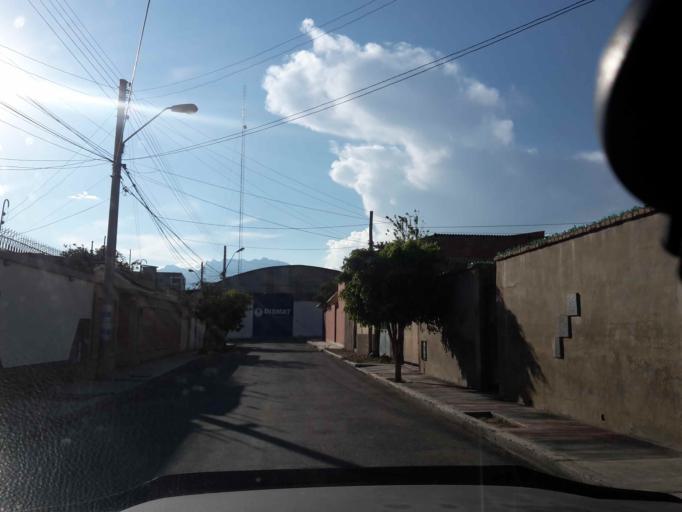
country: BO
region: Cochabamba
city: Cochabamba
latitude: -17.3478
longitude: -66.1958
